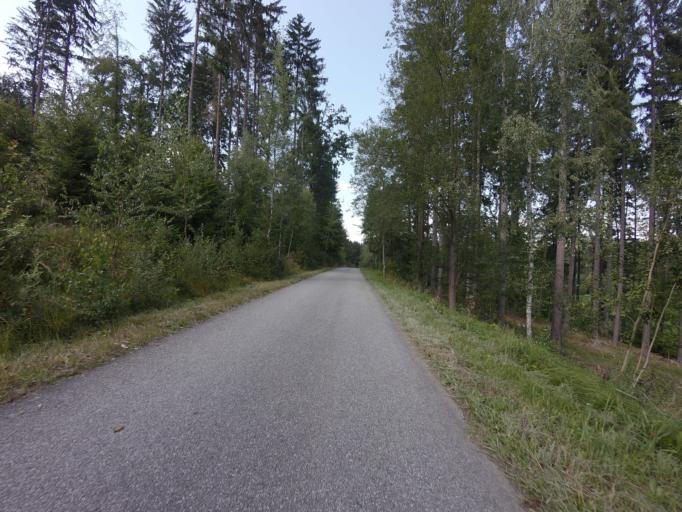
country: CZ
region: Jihocesky
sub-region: Okres Ceske Budejovice
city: Hluboka nad Vltavou
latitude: 49.1048
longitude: 14.4610
